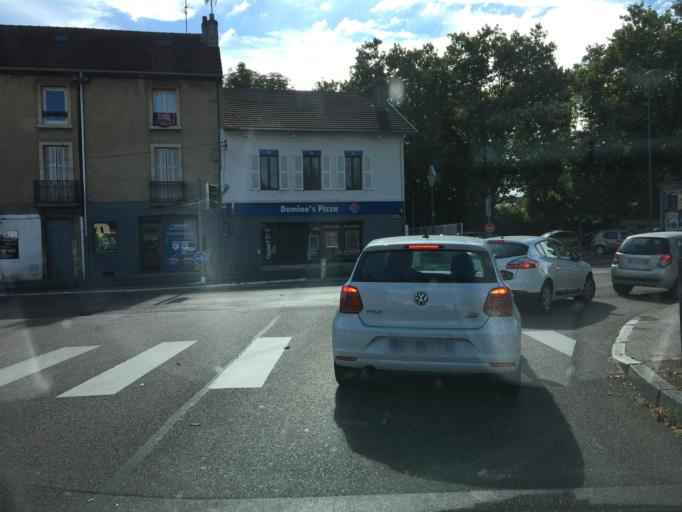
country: FR
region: Bourgogne
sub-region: Departement de la Cote-d'Or
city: Longvic
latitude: 47.3129
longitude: 5.0511
